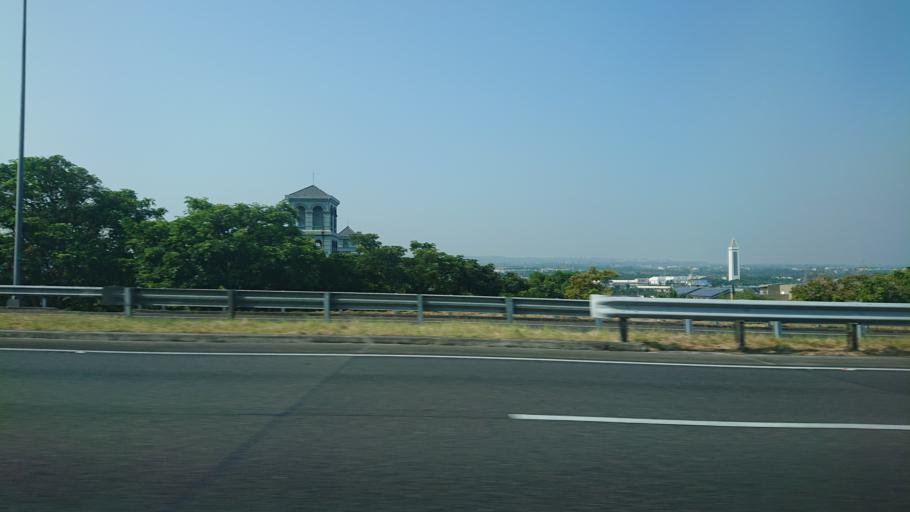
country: TW
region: Taiwan
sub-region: Nantou
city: Nantou
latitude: 23.8490
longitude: 120.7036
